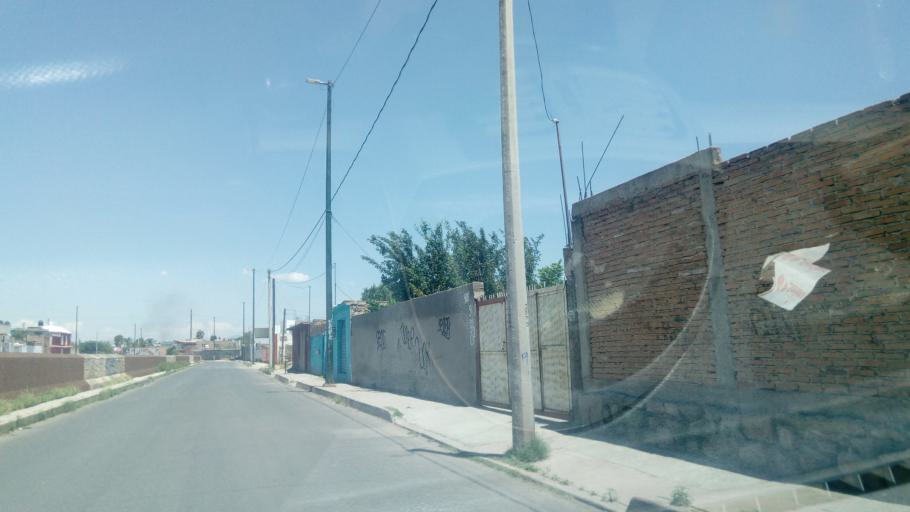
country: MX
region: Durango
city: Victoria de Durango
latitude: 24.0179
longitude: -104.6353
